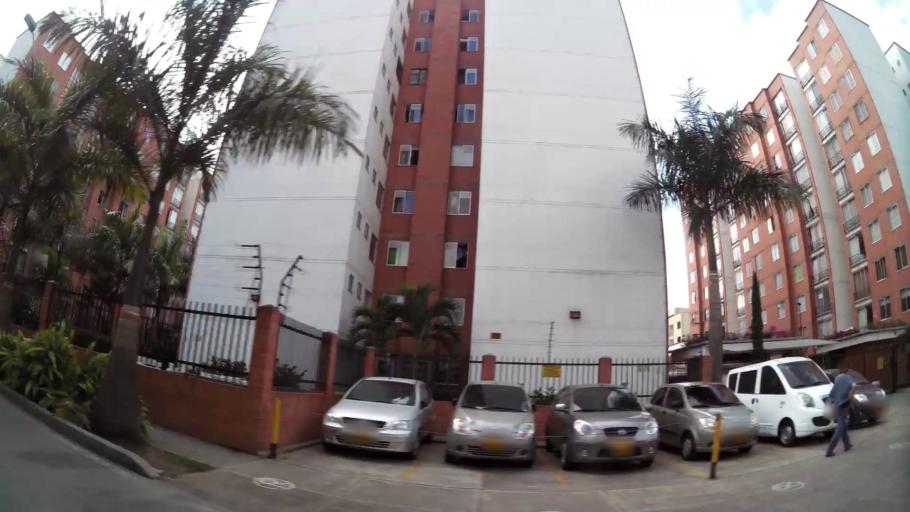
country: CO
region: Valle del Cauca
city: Cali
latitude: 3.4681
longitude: -76.5203
